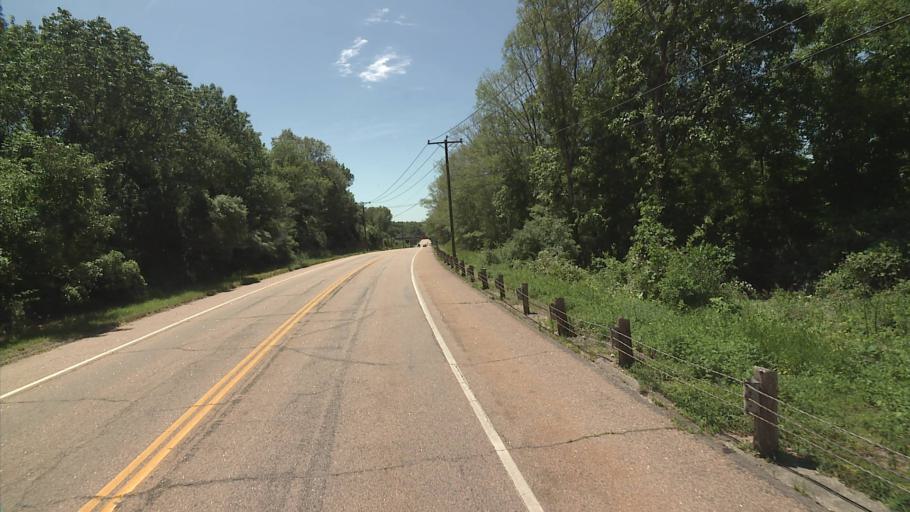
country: US
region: Connecticut
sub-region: New London County
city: Pawcatuck
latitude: 41.4234
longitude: -71.8448
